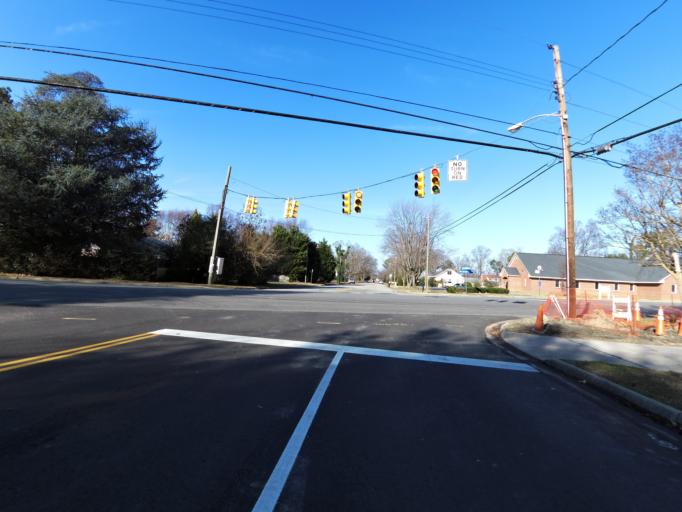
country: US
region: Virginia
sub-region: City of Hampton
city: Hampton
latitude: 37.0071
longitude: -76.3699
